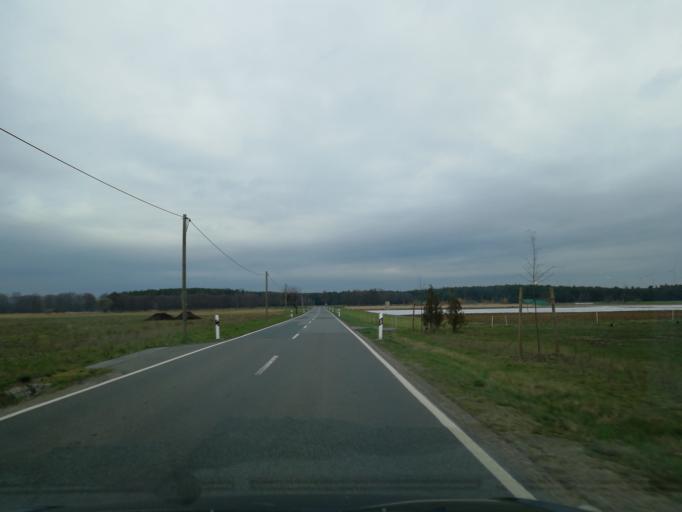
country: DE
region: Brandenburg
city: Vetschau
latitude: 51.7299
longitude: 14.0539
